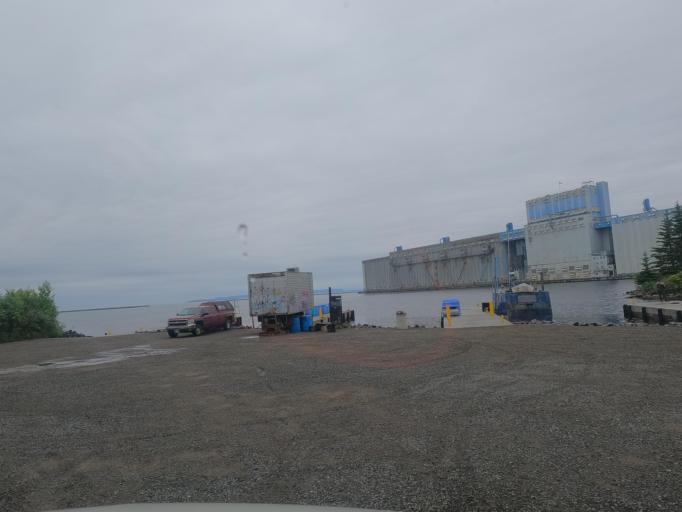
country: CA
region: Ontario
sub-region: Thunder Bay District
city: Thunder Bay
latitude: 48.4523
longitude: -89.1829
